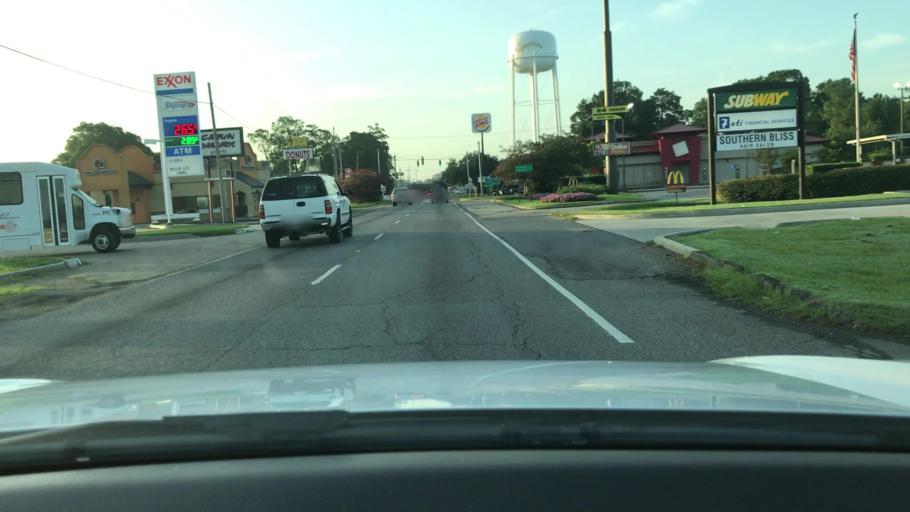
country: US
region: Louisiana
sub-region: Iberville Parish
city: Plaquemine
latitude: 30.2820
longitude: -91.2287
